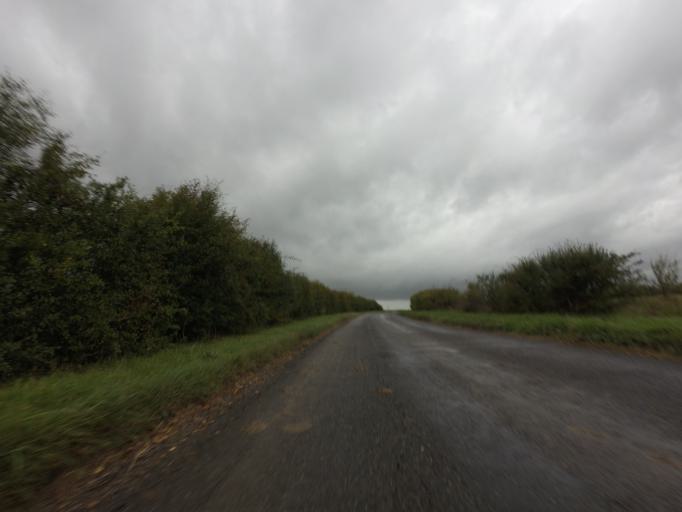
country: GB
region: England
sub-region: Cambridgeshire
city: Wimpole
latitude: 52.1815
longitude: -0.0408
